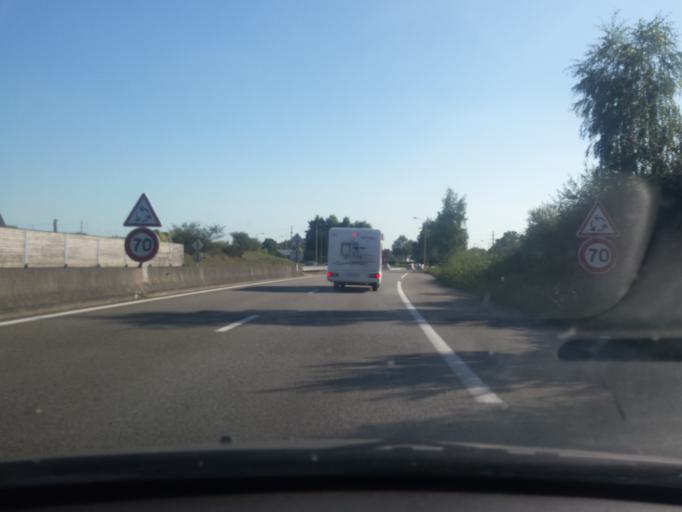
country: FR
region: Brittany
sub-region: Departement du Morbihan
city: Saint-Ave
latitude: 47.6859
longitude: -2.7664
